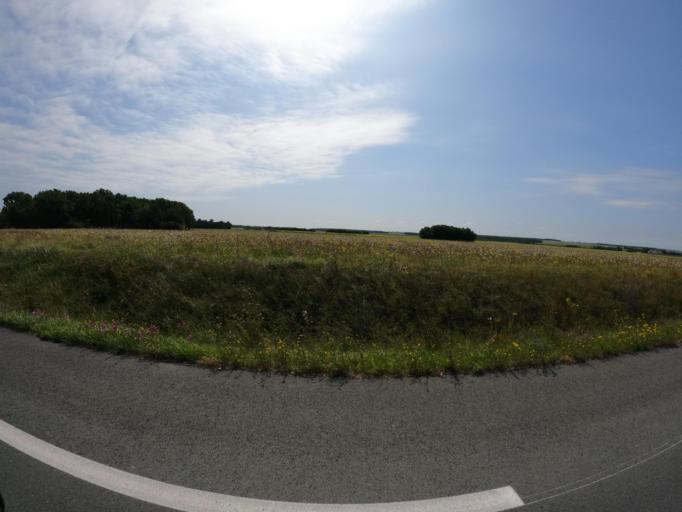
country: FR
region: Poitou-Charentes
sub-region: Departement des Deux-Sevres
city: Mauze-sur-le-Mignon
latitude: 46.2159
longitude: -0.6172
